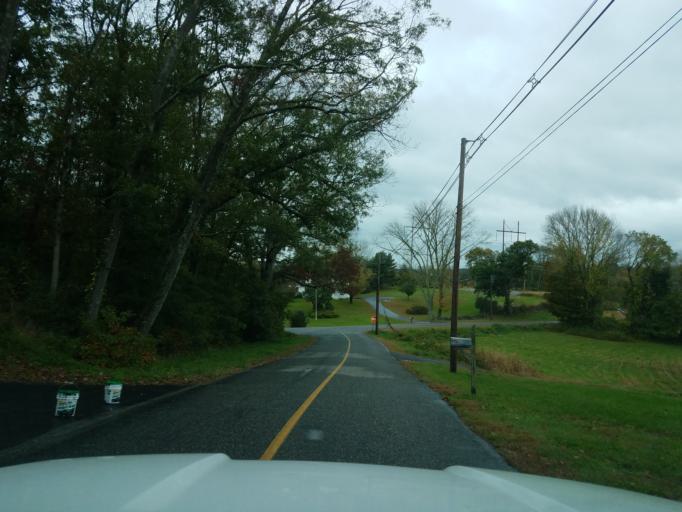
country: US
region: Connecticut
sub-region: Tolland County
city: South Coventry
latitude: 41.6973
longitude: -72.2977
